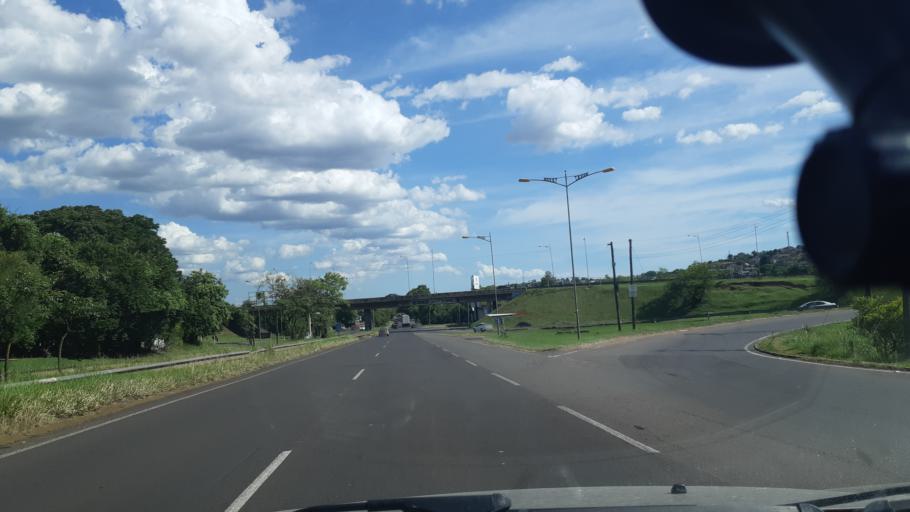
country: BR
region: Rio Grande do Sul
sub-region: Novo Hamburgo
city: Novo Hamburgo
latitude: -29.6558
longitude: -51.1445
